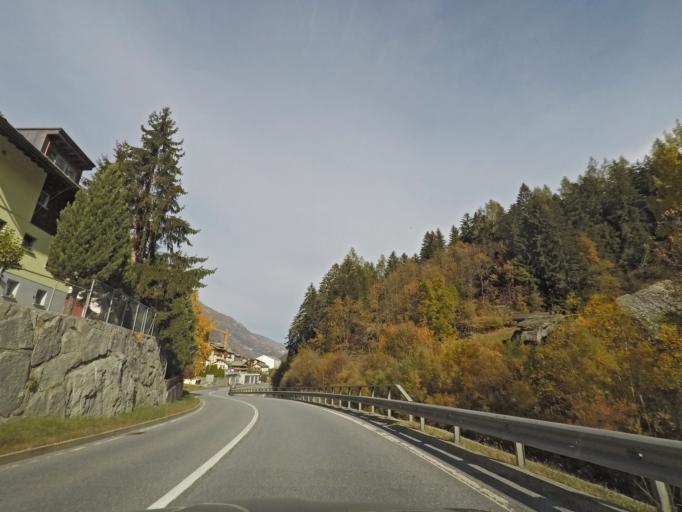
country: CH
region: Valais
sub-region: Visp District
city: Sankt Niklaus
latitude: 46.1728
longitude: 7.8005
